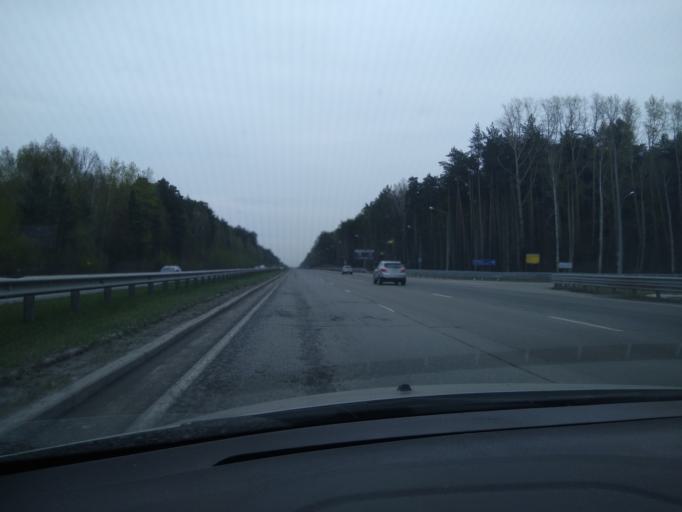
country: RU
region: Sverdlovsk
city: Istok
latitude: 56.8176
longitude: 60.7296
